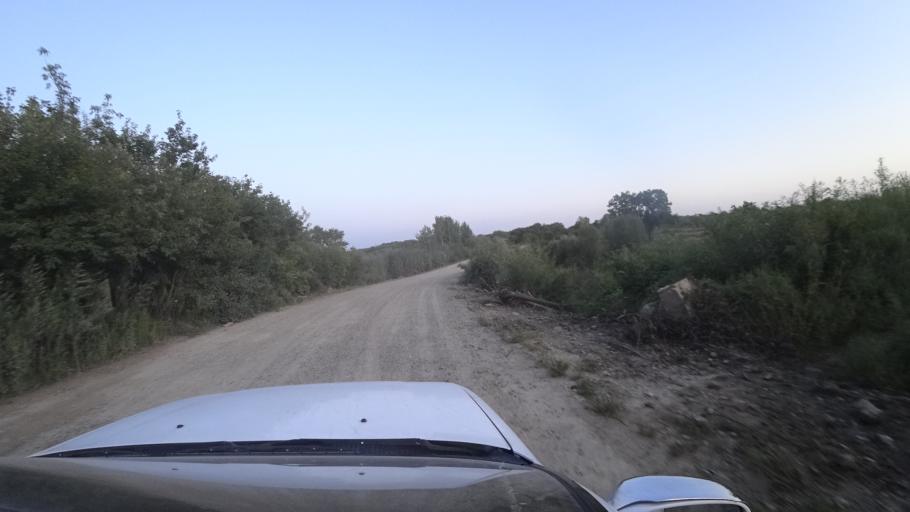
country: RU
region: Primorskiy
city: Dal'nerechensk
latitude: 45.9424
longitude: 133.7608
